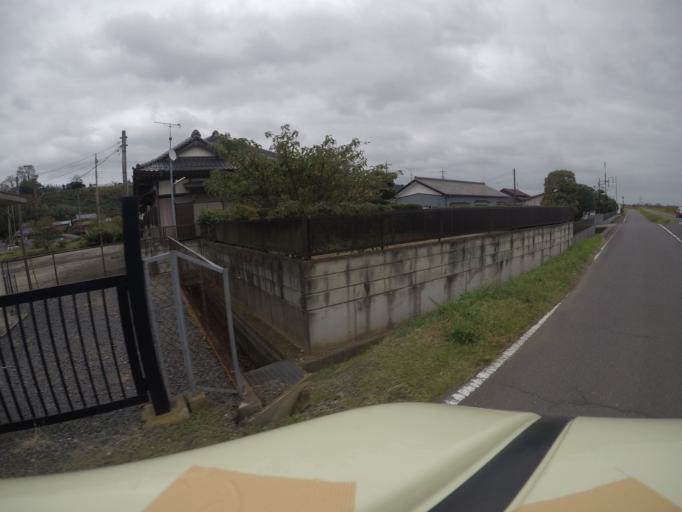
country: JP
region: Ibaraki
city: Itako
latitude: 35.9715
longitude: 140.5014
